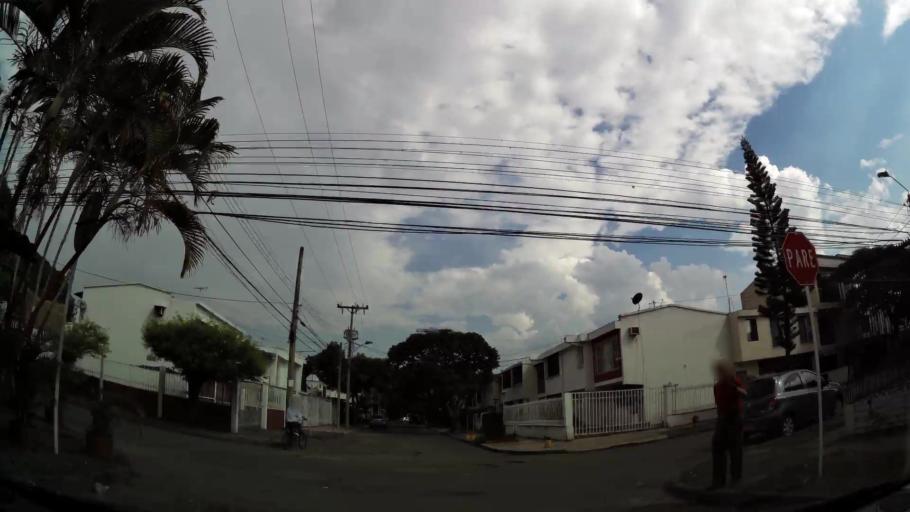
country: CO
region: Valle del Cauca
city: Cali
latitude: 3.4811
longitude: -76.5147
